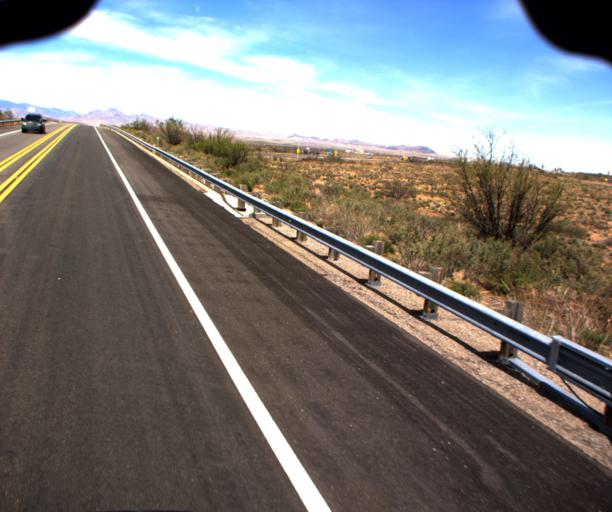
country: US
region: Arizona
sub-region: Cochise County
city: Willcox
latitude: 32.3057
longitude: -109.7968
